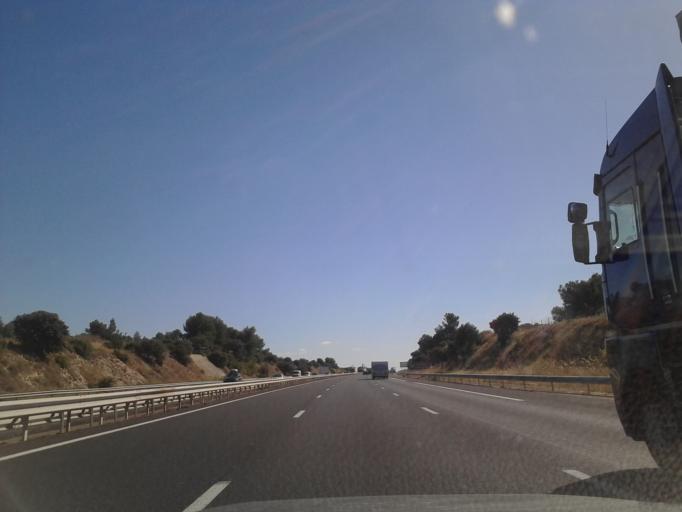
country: FR
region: Languedoc-Roussillon
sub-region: Departement de l'Herault
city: Vendres
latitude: 43.2977
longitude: 3.2030
